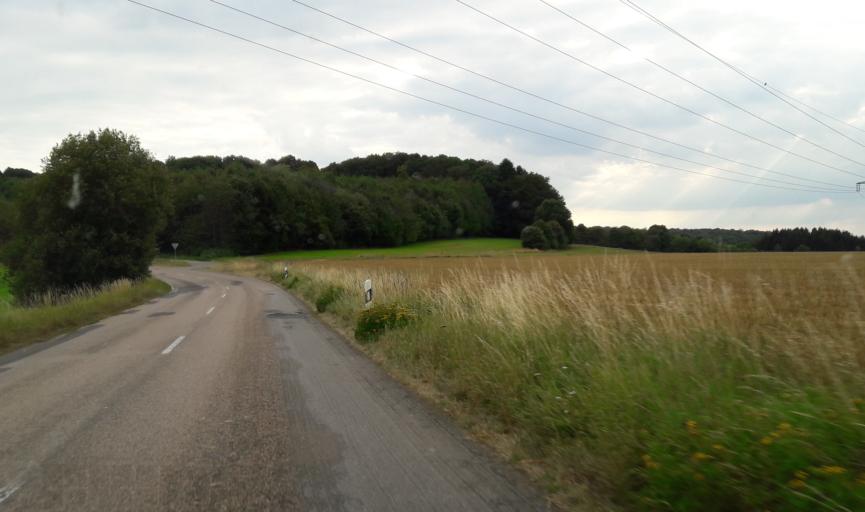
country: DE
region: Saarland
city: Tholey
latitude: 49.4638
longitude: 7.0304
